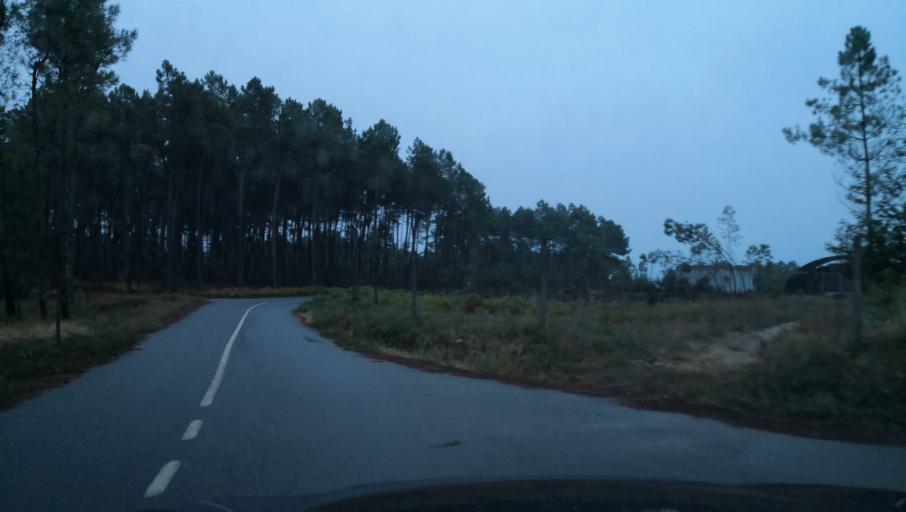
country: PT
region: Vila Real
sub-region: Sabrosa
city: Sabrosa
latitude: 41.2704
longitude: -7.5926
